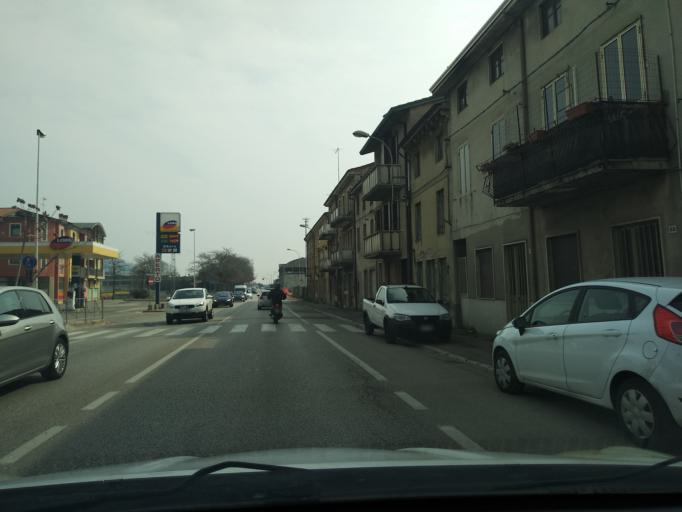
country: IT
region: Veneto
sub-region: Provincia di Vicenza
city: Chiampo
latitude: 45.5400
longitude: 11.2895
